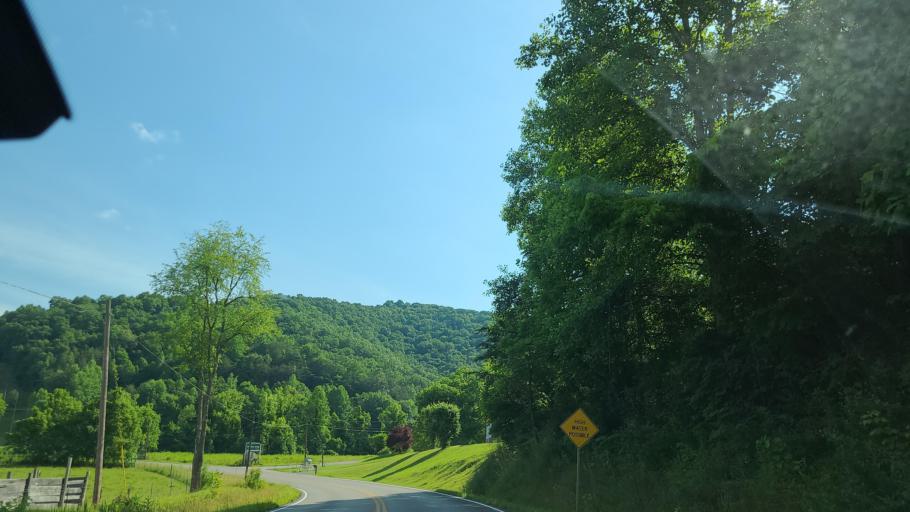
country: US
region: Kentucky
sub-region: Bell County
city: Pineville
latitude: 36.7523
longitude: -83.7822
